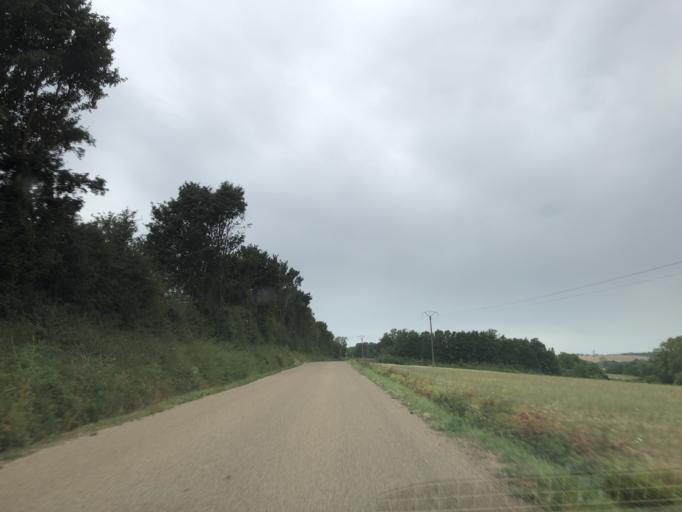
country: FR
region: Bourgogne
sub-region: Departement de l'Yonne
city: Charny
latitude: 47.9498
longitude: 3.1343
